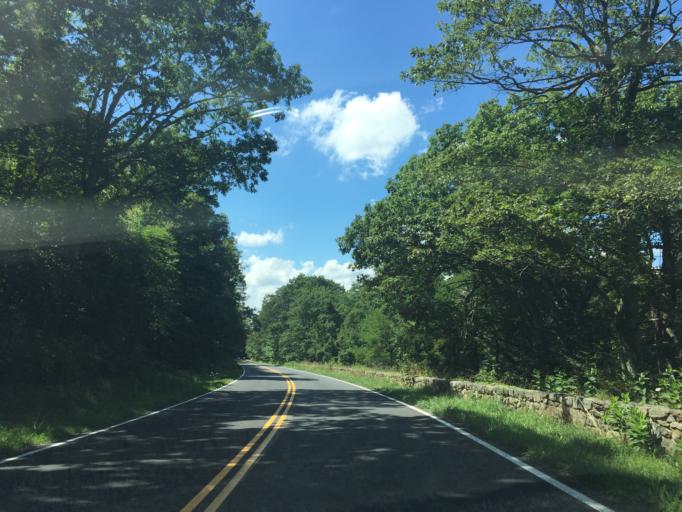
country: US
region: Virginia
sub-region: Rappahannock County
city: Washington
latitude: 38.7531
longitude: -78.2953
